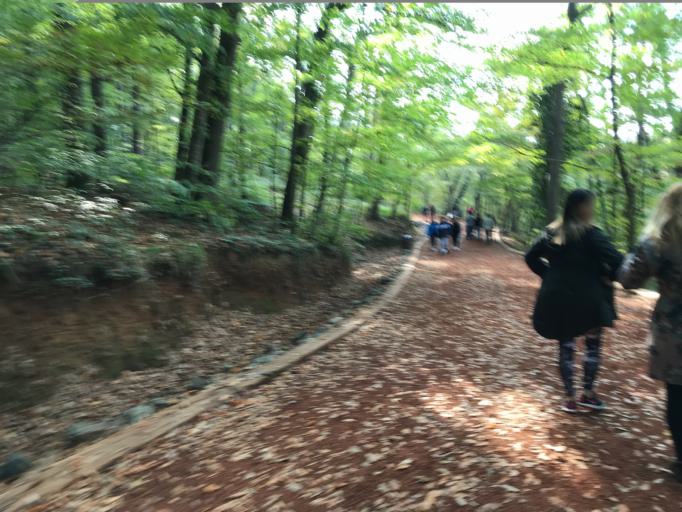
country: TR
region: Istanbul
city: Kemerburgaz
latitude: 41.1807
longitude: 28.9613
